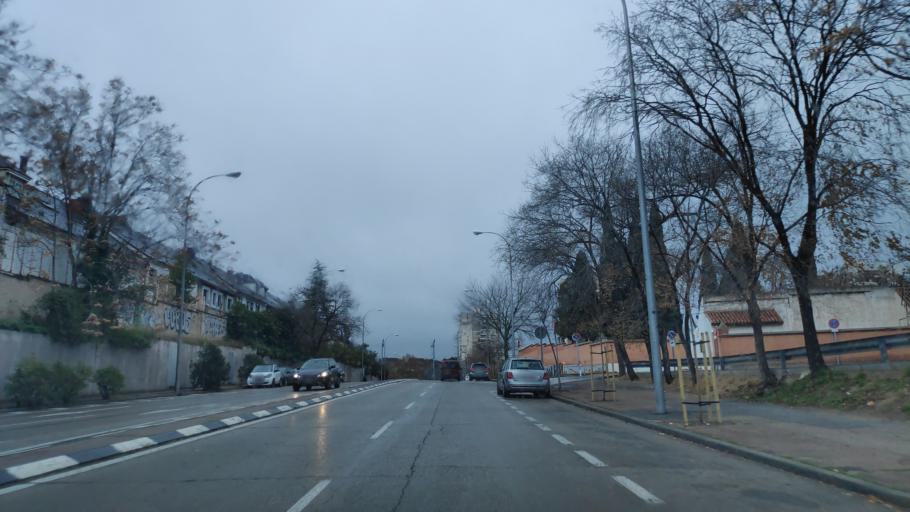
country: ES
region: Madrid
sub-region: Provincia de Madrid
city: Ciudad Lineal
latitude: 40.4614
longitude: -3.6403
